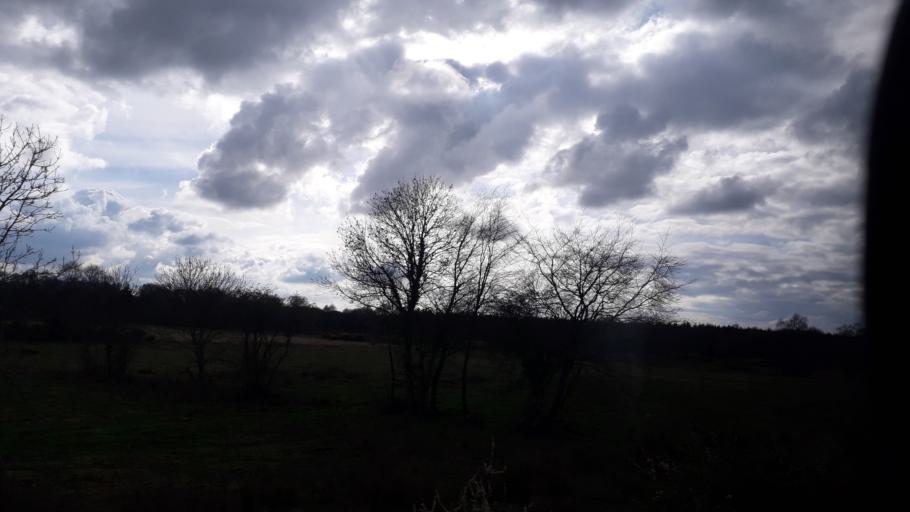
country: IE
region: Leinster
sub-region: An Iarmhi
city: Rathwire
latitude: 53.4930
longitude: -7.2212
